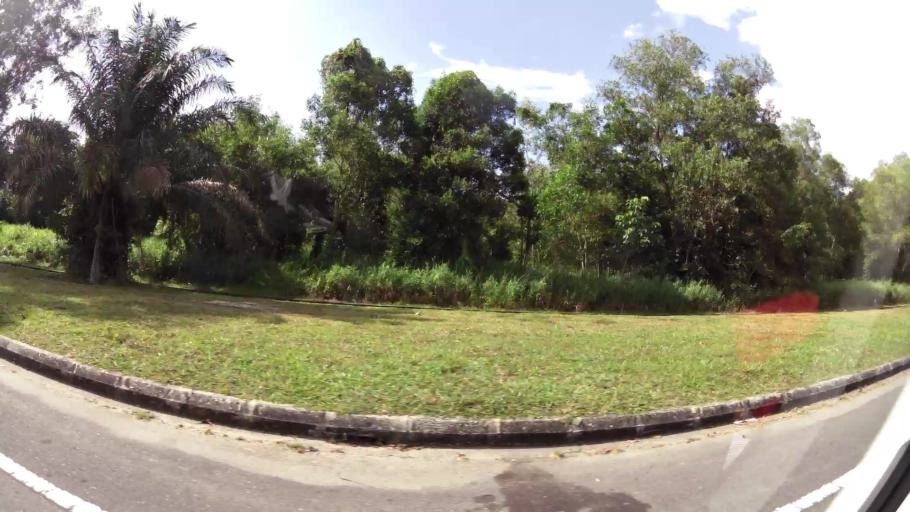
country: BN
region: Brunei and Muara
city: Bandar Seri Begawan
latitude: 4.9513
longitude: 114.9487
